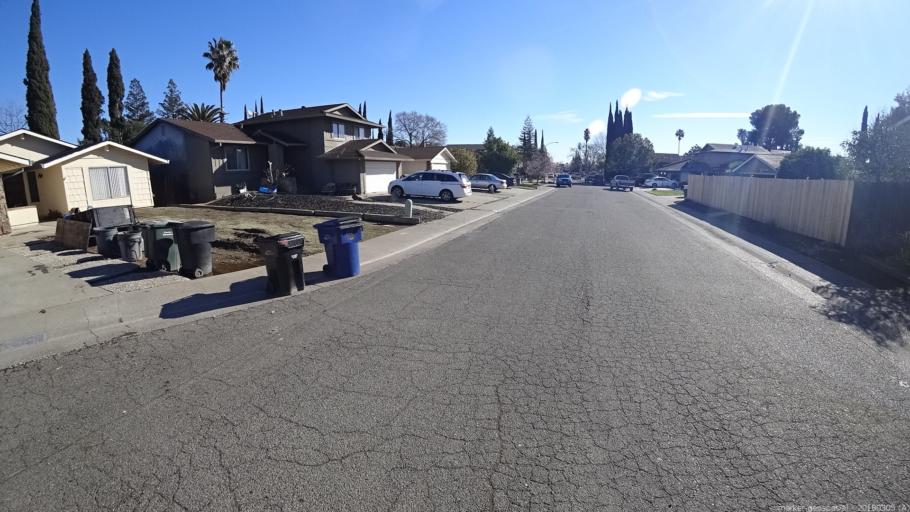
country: US
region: California
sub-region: Sacramento County
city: Florin
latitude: 38.4844
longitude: -121.4151
